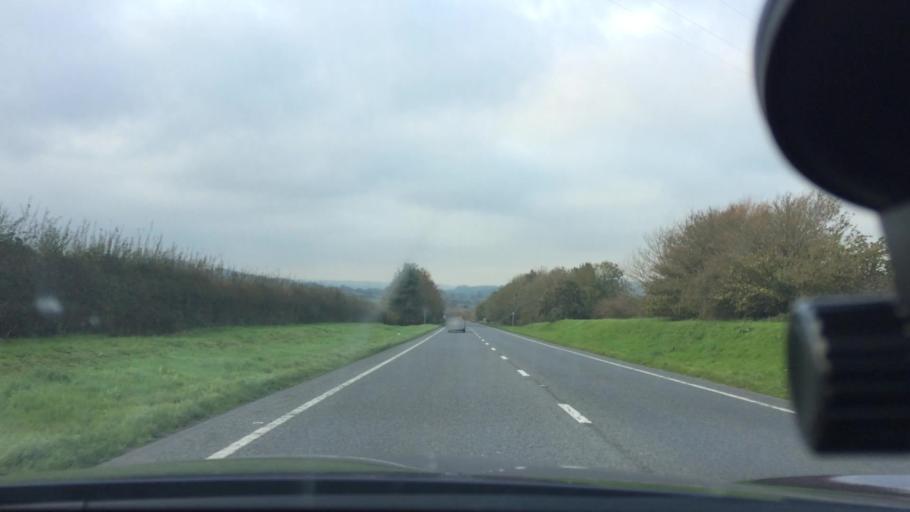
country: GB
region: England
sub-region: Devon
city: Axminster
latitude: 50.7720
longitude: -3.0083
